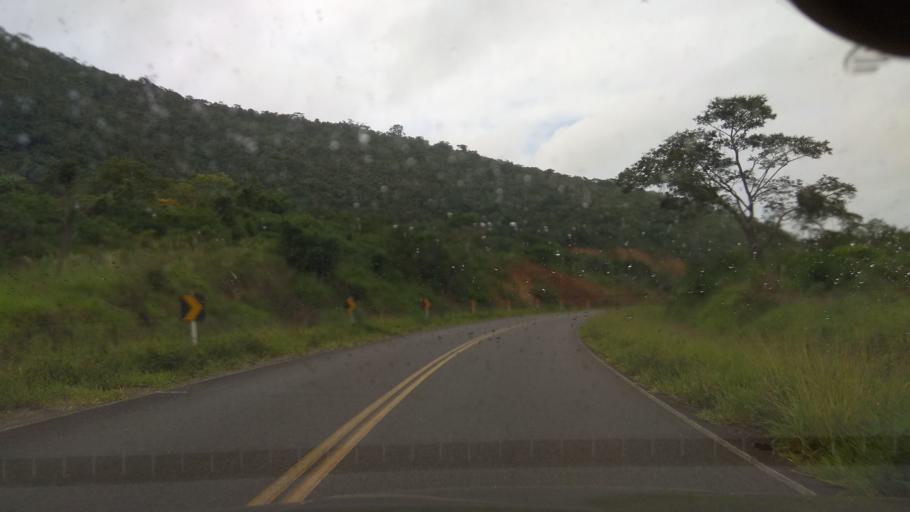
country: BR
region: Bahia
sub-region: Ubaira
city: Ubaira
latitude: -13.2377
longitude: -39.7397
